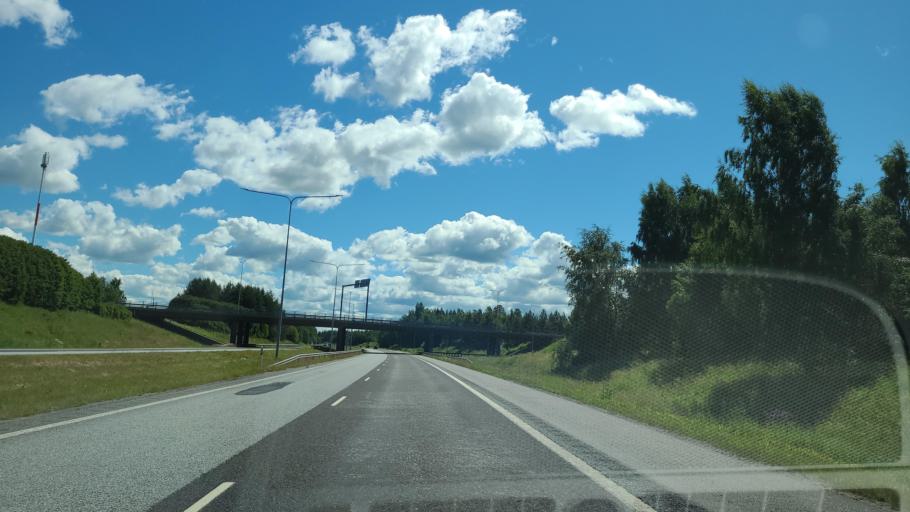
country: FI
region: Ostrobothnia
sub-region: Vaasa
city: Ristinummi
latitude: 63.0294
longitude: 21.7539
